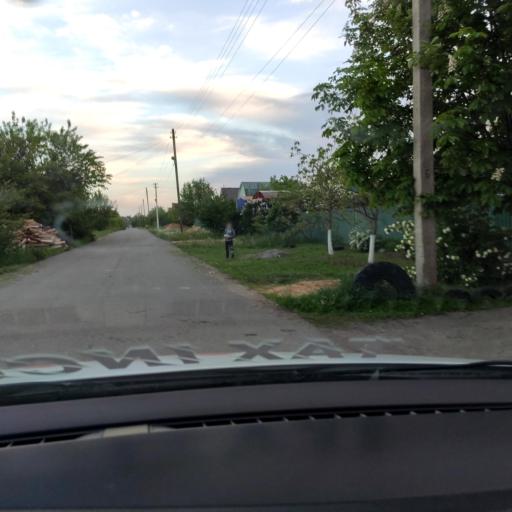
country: RU
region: Voronezj
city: Maslovka
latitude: 51.4447
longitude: 39.2344
